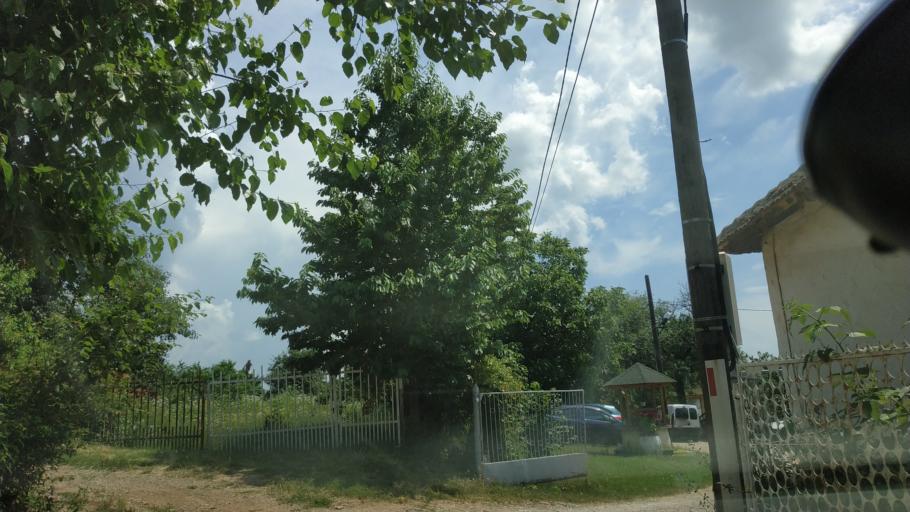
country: RS
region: Central Serbia
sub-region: Nisavski Okrug
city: Aleksinac
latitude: 43.5982
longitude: 21.6960
